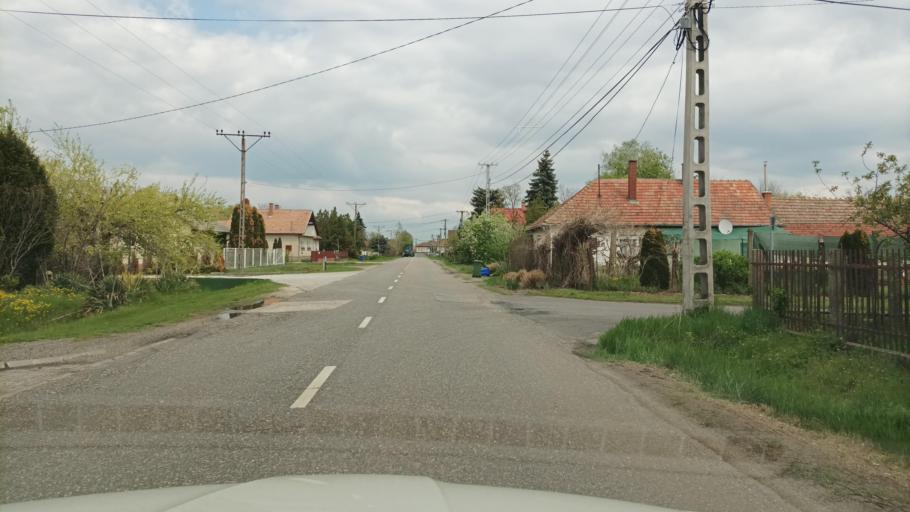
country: HU
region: Pest
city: Tortel
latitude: 47.1172
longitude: 19.9235
